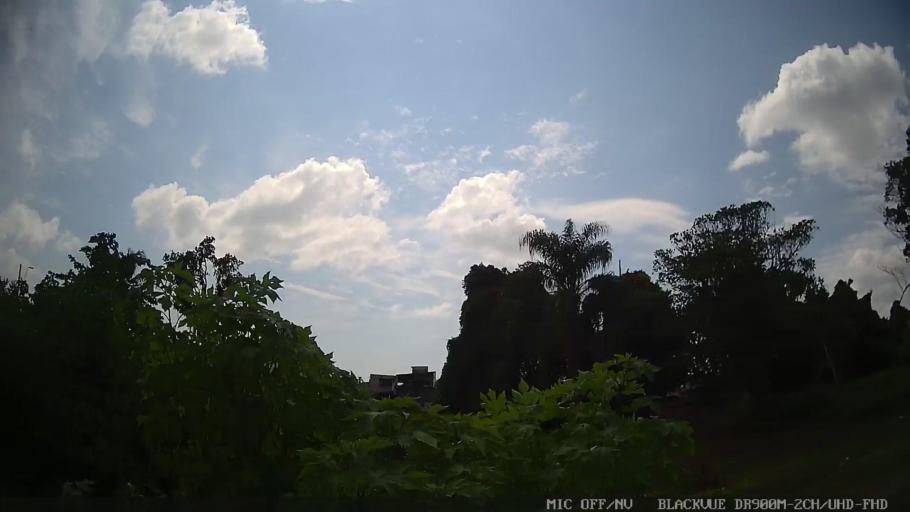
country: BR
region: Sao Paulo
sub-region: Caraguatatuba
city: Caraguatatuba
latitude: -23.6745
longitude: -45.4494
